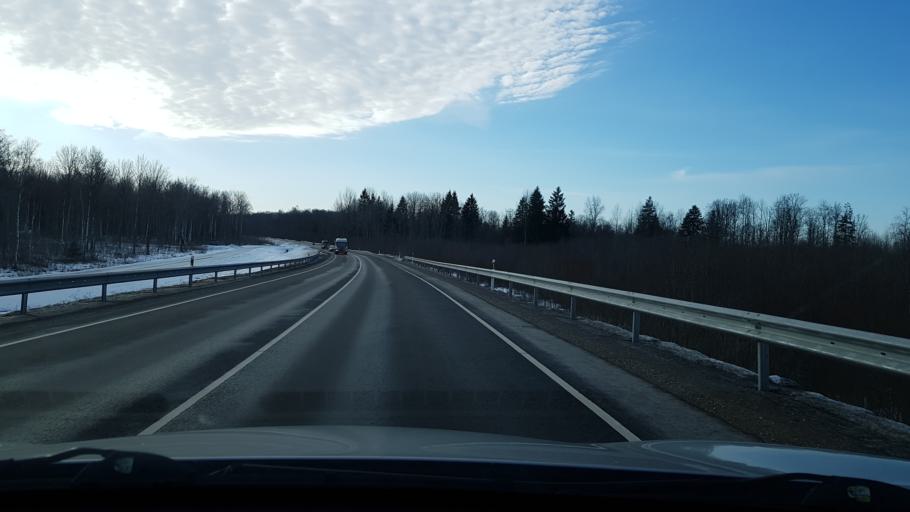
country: EE
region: Viljandimaa
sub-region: Viljandi linn
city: Viljandi
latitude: 58.3866
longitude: 25.5607
